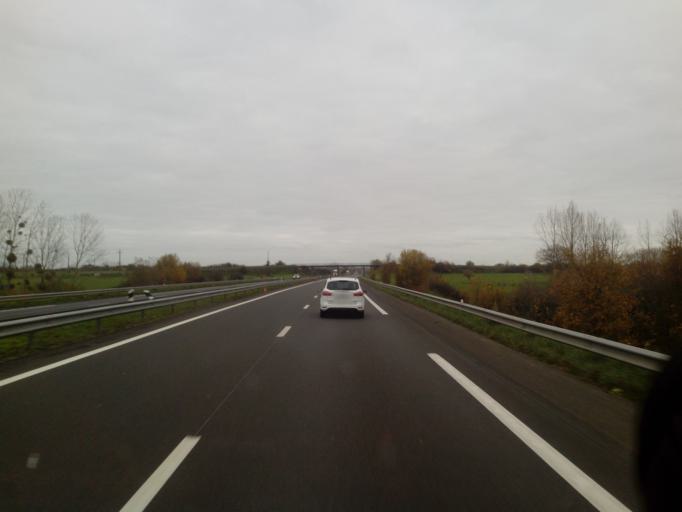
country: FR
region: Pays de la Loire
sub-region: Departement de Maine-et-Loire
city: Roussay
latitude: 47.1159
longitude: -1.0634
